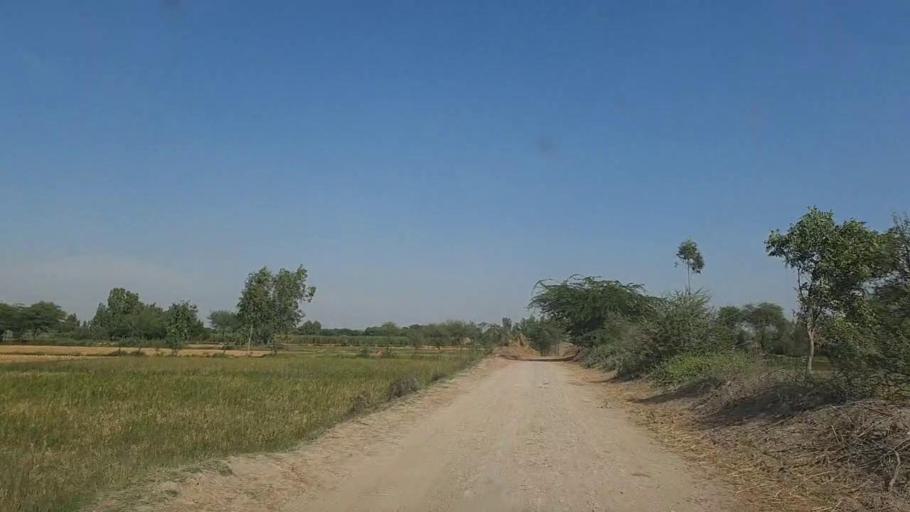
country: PK
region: Sindh
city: Mirpur Batoro
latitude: 24.7981
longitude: 68.2747
